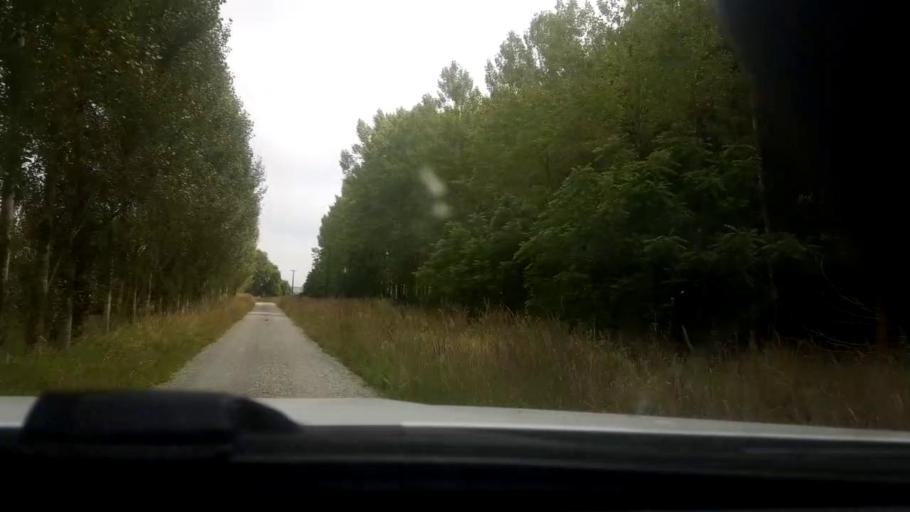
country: NZ
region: Canterbury
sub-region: Timaru District
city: Pleasant Point
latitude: -44.3267
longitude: 171.1961
